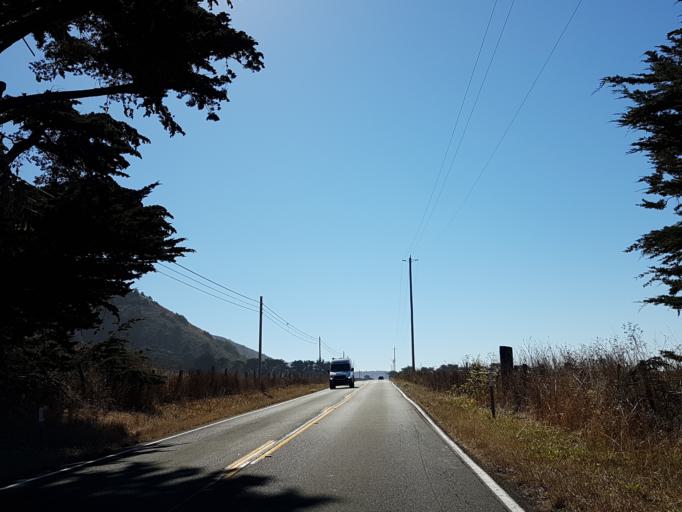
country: US
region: California
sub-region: Mendocino County
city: Boonville
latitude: 39.0880
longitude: -123.7001
